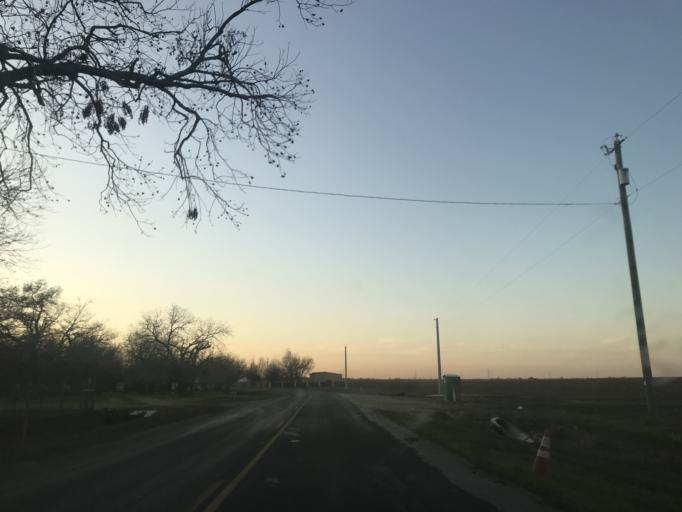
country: US
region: Texas
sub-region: Williamson County
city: Hutto
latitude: 30.4989
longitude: -97.5056
